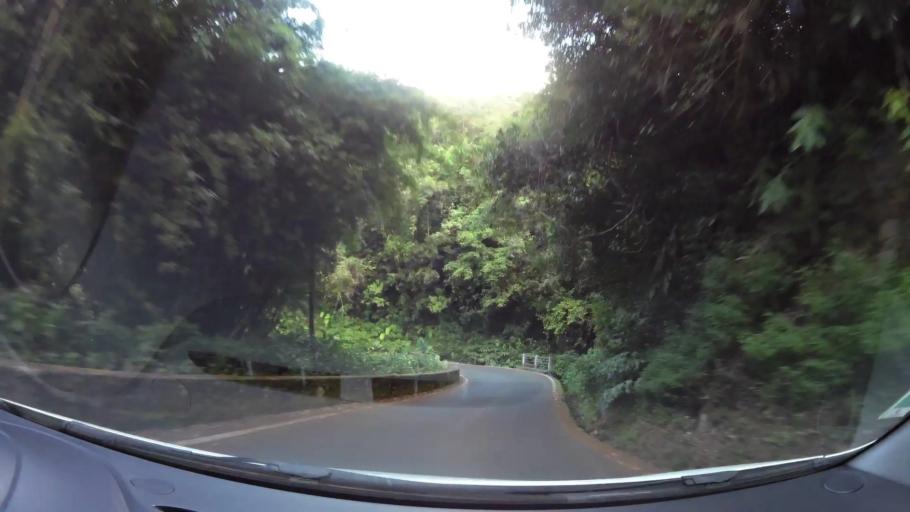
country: RE
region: Reunion
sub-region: Reunion
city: Saint-Denis
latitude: -20.9258
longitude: 55.4416
